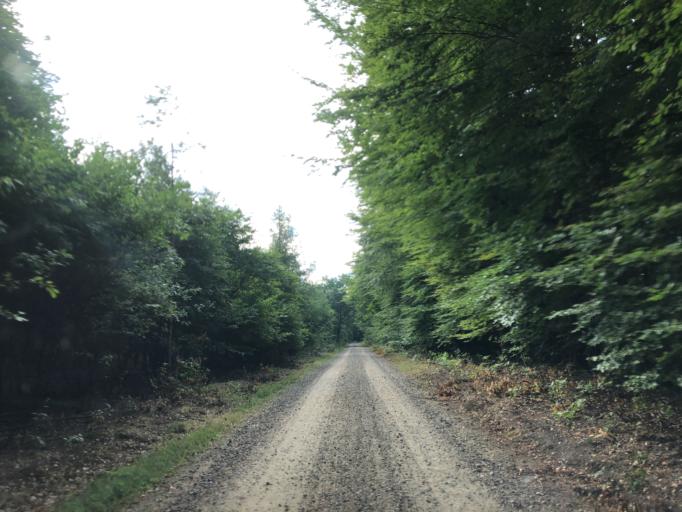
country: DK
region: Central Jutland
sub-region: Holstebro Kommune
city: Ulfborg
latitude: 56.1666
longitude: 8.3969
